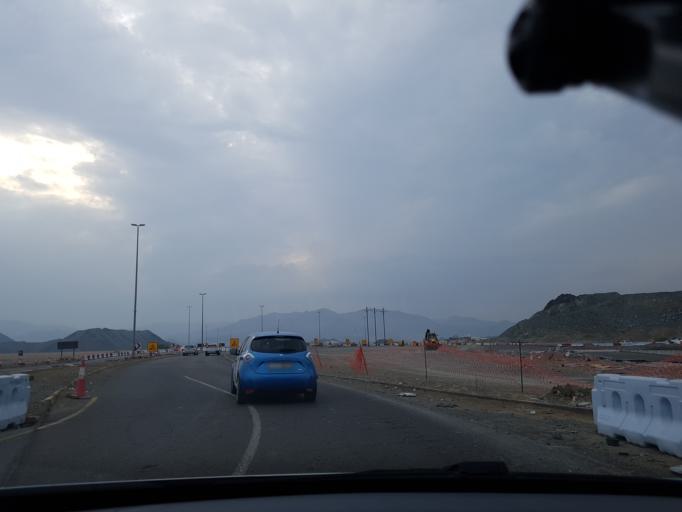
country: AE
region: Al Fujayrah
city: Al Fujayrah
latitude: 25.1219
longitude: 56.3162
